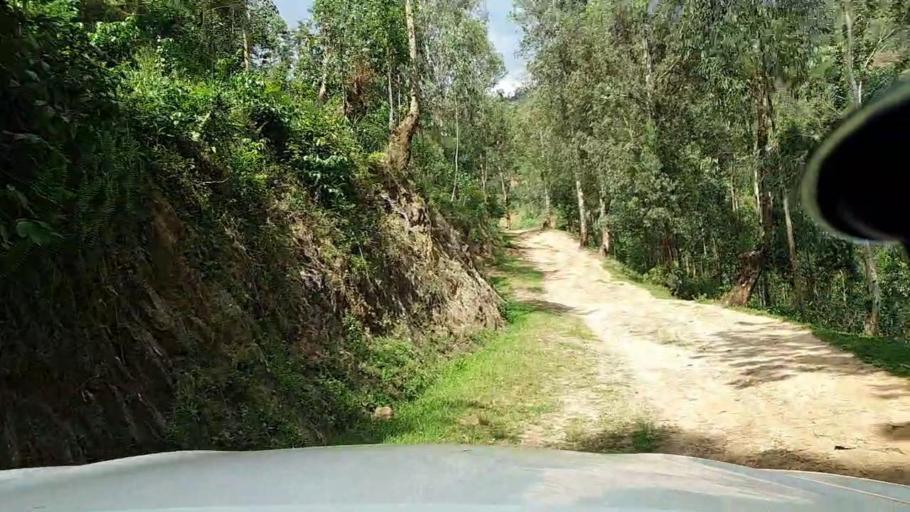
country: RW
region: Southern Province
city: Gitarama
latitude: -1.8225
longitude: 29.8007
